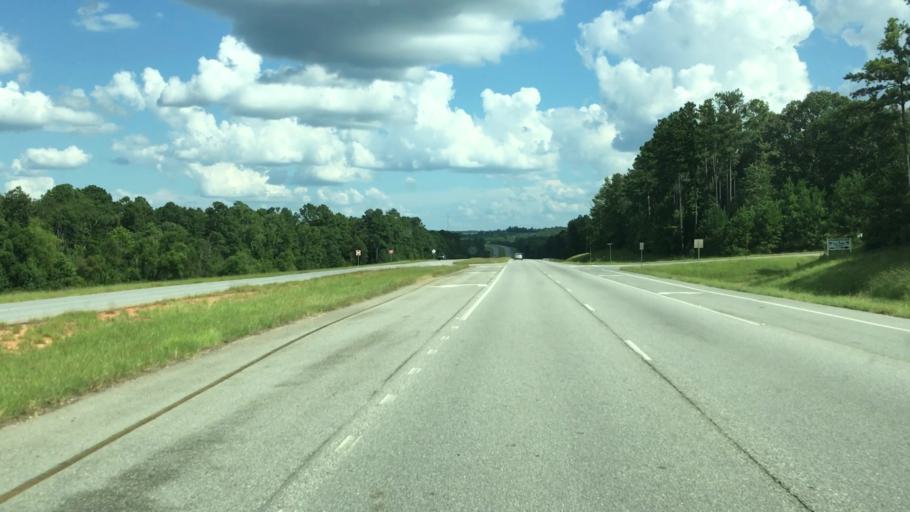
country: US
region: Georgia
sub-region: Wilkinson County
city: Irwinton
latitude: 32.7073
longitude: -83.1319
